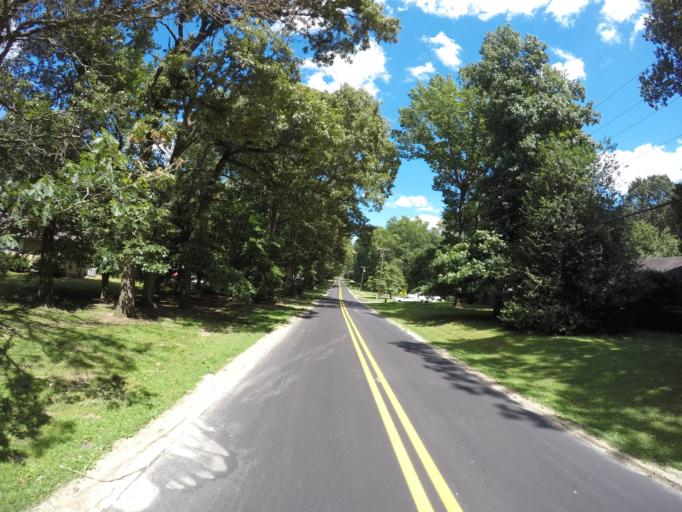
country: US
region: Delaware
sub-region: Sussex County
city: Milford
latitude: 38.9311
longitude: -75.4161
